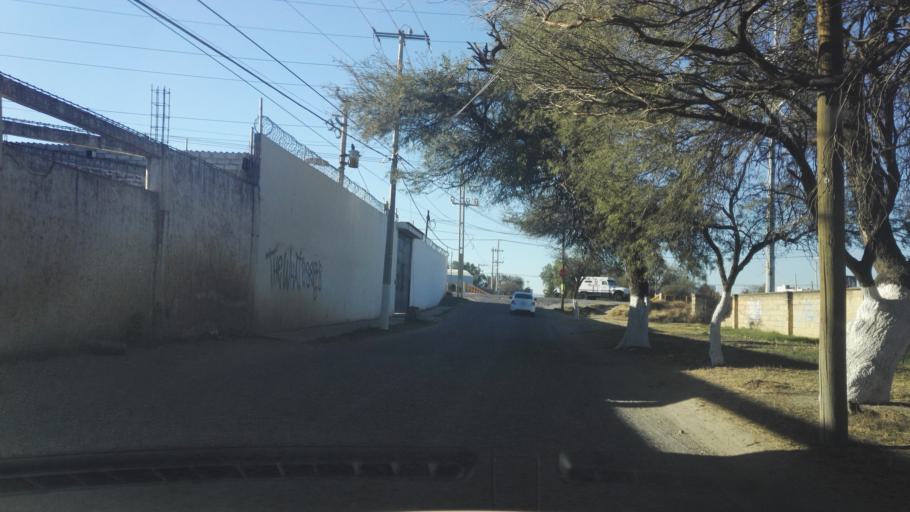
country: MX
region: Guanajuato
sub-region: Leon
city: Fraccionamiento Paraiso Real
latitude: 21.0718
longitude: -101.6009
